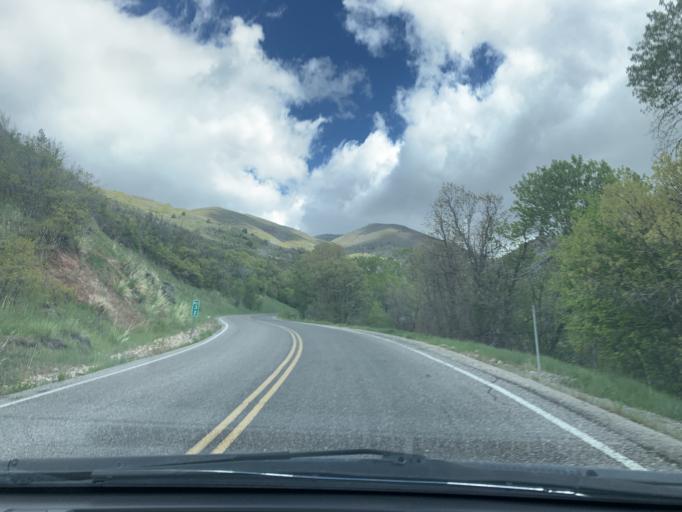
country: US
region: Utah
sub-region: Juab County
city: Nephi
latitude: 39.7701
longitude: -111.7048
